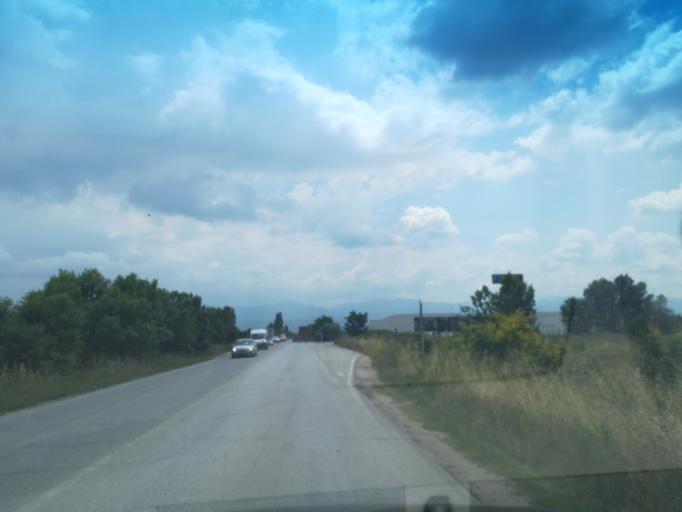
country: BG
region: Plovdiv
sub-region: Obshtina Plovdiv
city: Plovdiv
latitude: 42.1661
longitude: 24.6766
